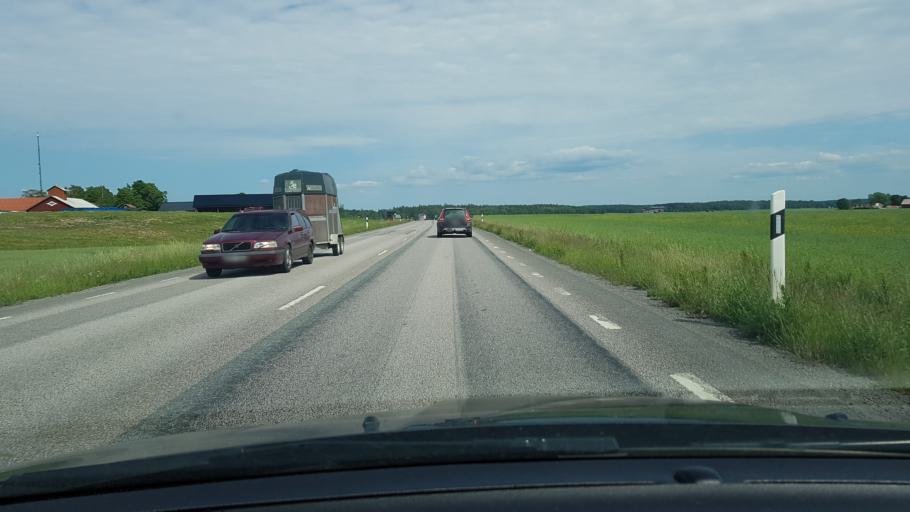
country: SE
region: Uppsala
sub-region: Uppsala Kommun
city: Saevja
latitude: 59.8446
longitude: 17.7472
